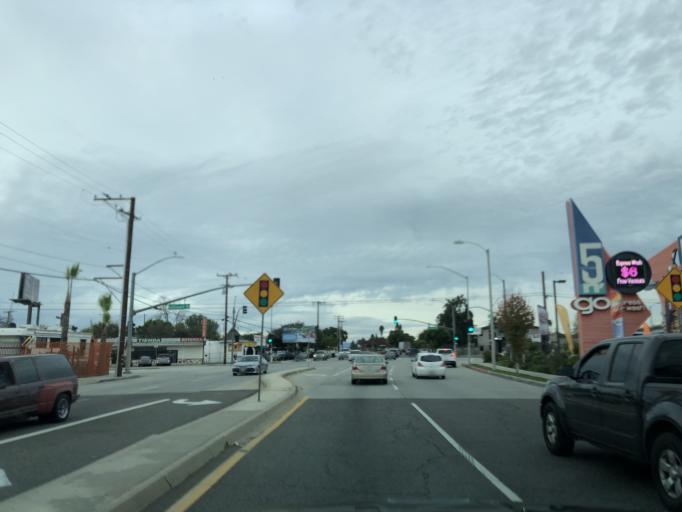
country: US
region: California
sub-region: Los Angeles County
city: La Mirada
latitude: 33.9180
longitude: -118.0467
